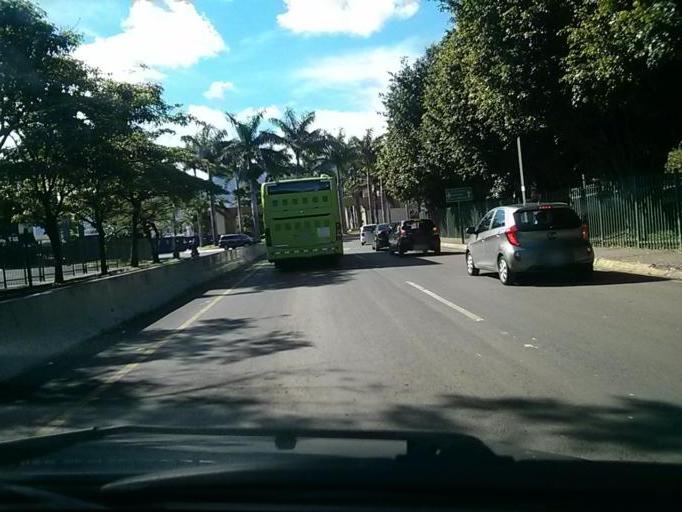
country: CR
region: San Jose
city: San Rafael
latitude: 9.9456
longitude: -84.1527
